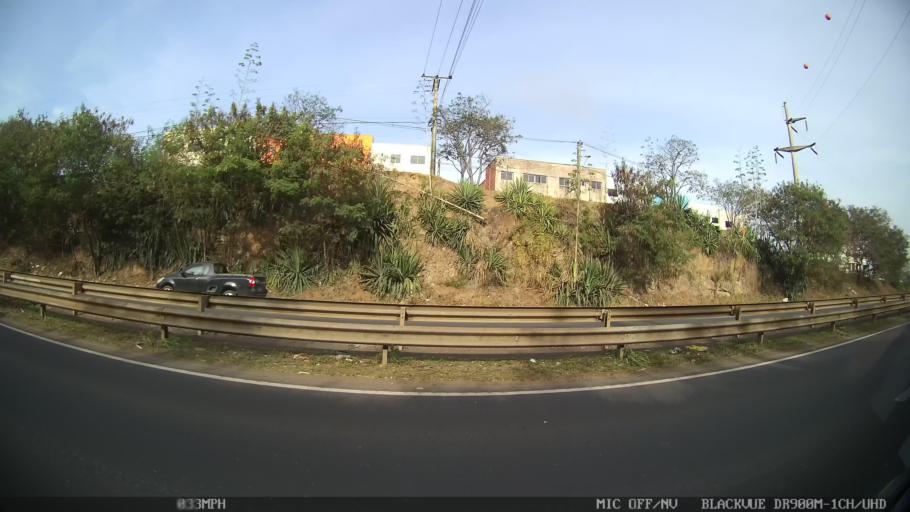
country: BR
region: Sao Paulo
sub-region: Piracicaba
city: Piracicaba
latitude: -22.6875
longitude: -47.6694
